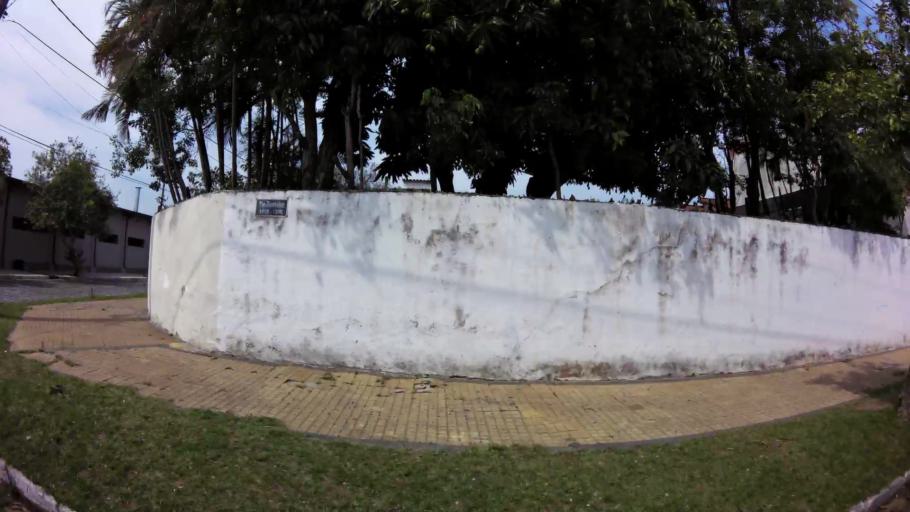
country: PY
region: Asuncion
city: Asuncion
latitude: -25.2645
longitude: -57.5834
